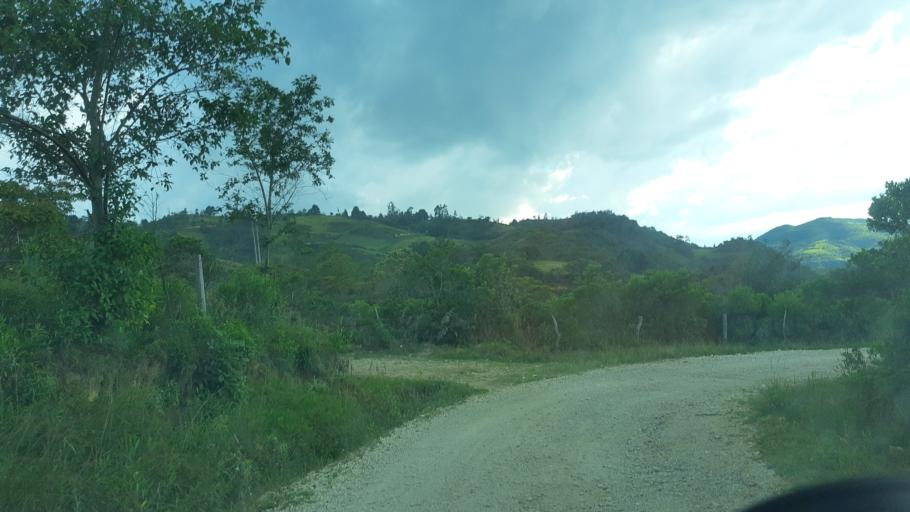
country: CO
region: Boyaca
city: Santa Sofia
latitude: 5.7449
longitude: -73.5638
